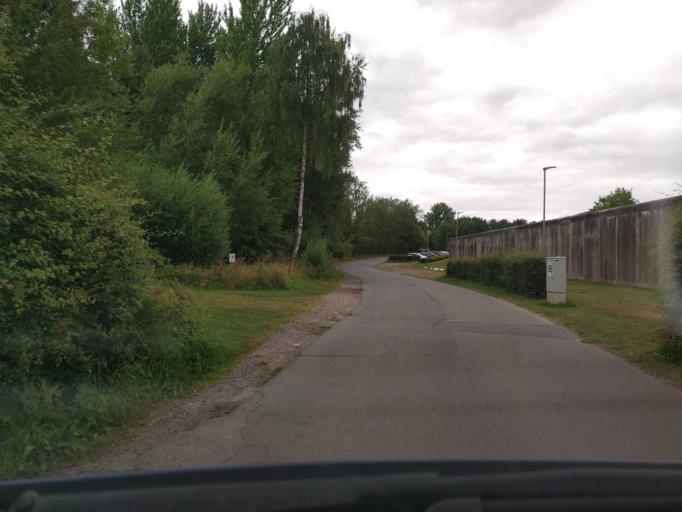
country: DE
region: Schleswig-Holstein
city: Schuby
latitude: 54.5158
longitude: 9.5176
